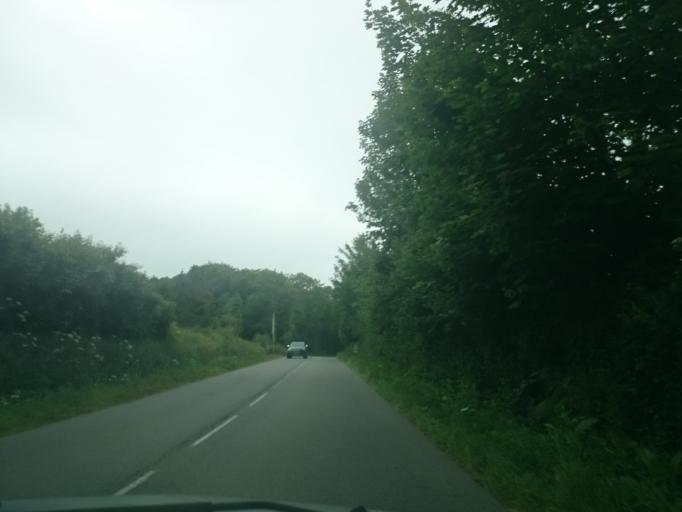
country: FR
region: Brittany
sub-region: Departement du Finistere
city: Lannilis
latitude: 48.5532
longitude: -4.5506
